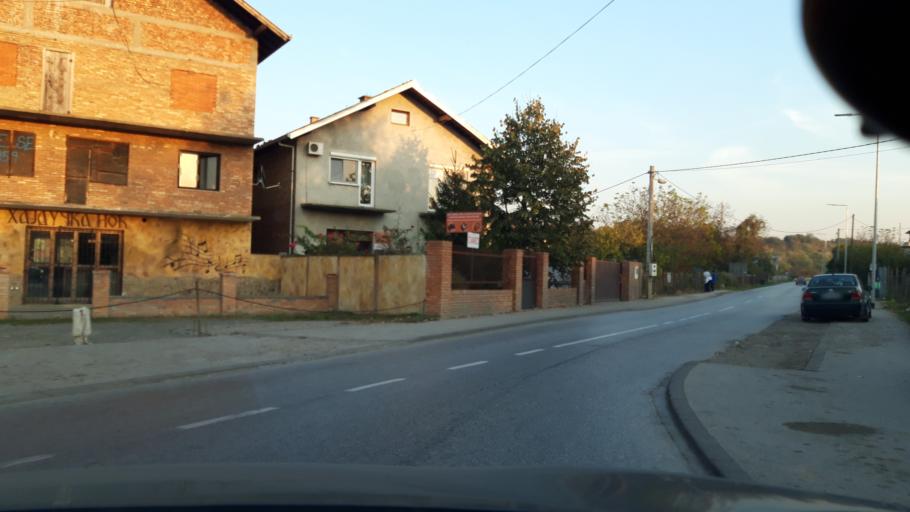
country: RS
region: Autonomna Pokrajina Vojvodina
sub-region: Juznobacki Okrug
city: Petrovaradin
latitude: 45.2327
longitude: 19.8849
